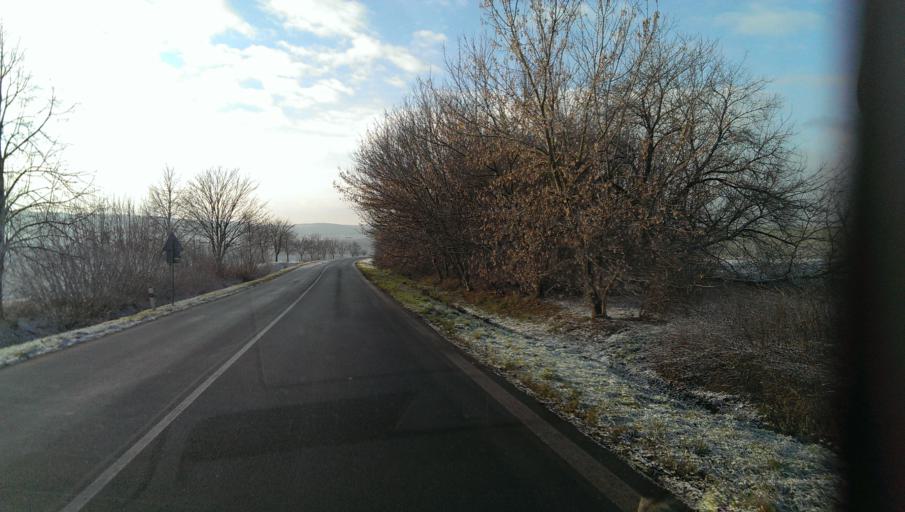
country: CZ
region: Ustecky
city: Budyne nad Ohri
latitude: 50.4121
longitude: 14.1772
